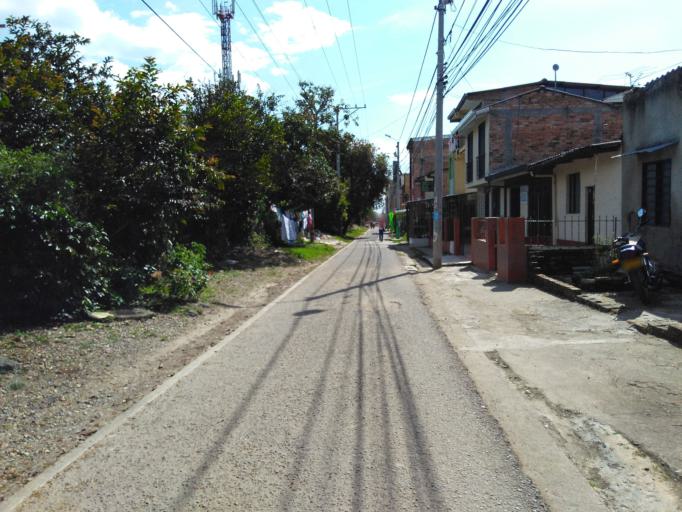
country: CO
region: Cauca
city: Popayan
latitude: 2.4525
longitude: -76.5960
